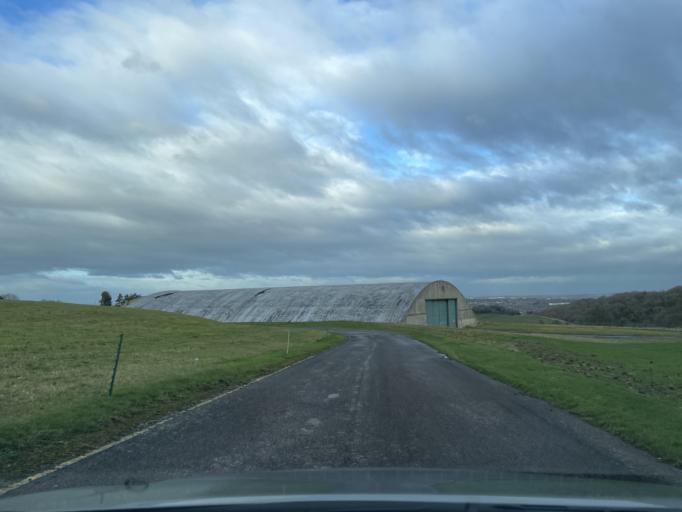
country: GB
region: England
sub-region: Borough of Swindon
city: Wroughton
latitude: 51.5085
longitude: -1.8114
